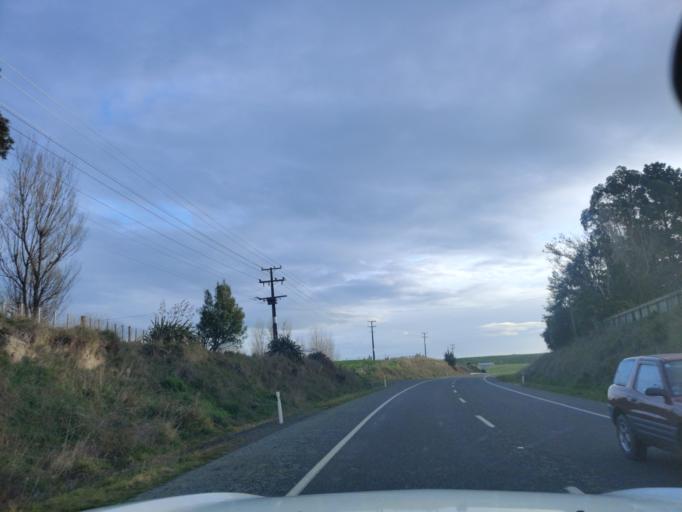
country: NZ
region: Manawatu-Wanganui
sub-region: Palmerston North City
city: Palmerston North
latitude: -40.4052
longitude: 175.6149
